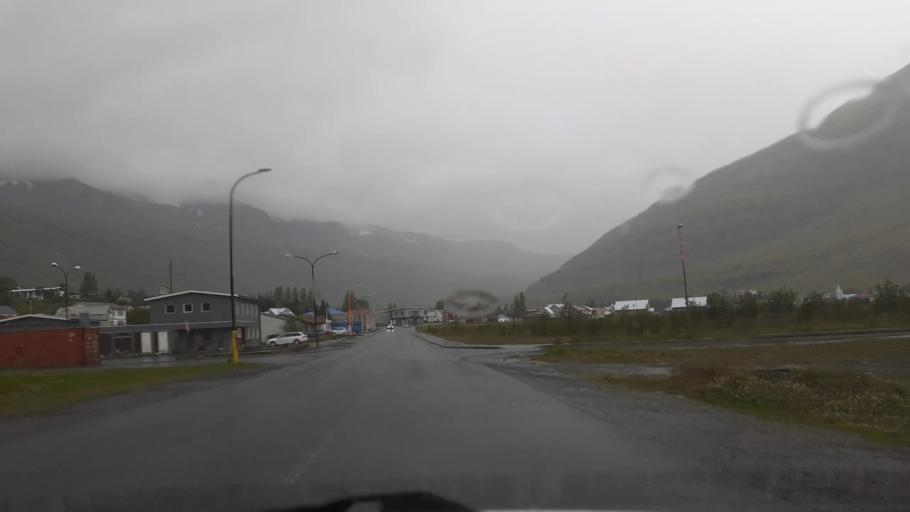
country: IS
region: East
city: Eskifjoerdur
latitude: 65.2634
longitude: -13.9967
